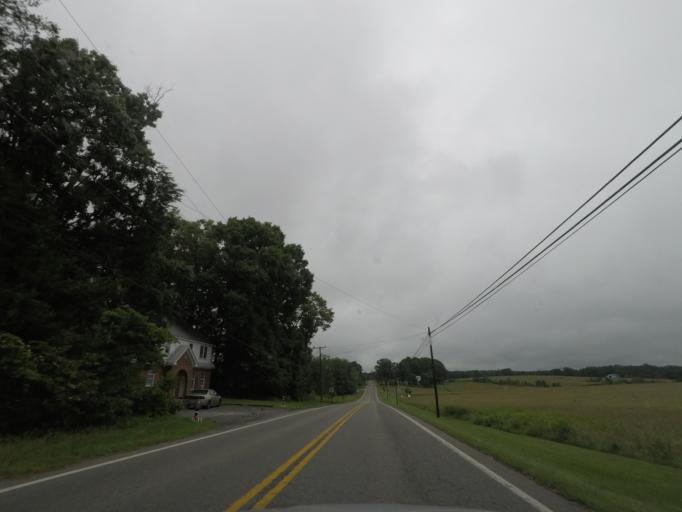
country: US
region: Virginia
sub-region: Fluvanna County
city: Weber City
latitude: 37.7700
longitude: -78.2549
